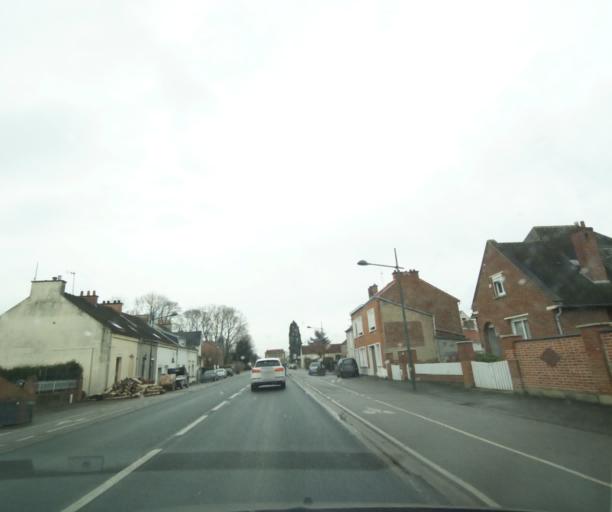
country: FR
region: Nord-Pas-de-Calais
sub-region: Departement du Nord
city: Haulchin
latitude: 50.3197
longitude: 3.4257
